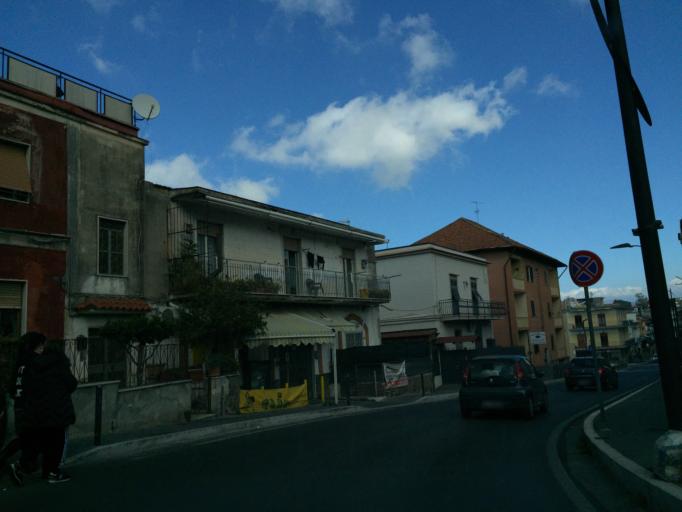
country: IT
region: Campania
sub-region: Provincia di Napoli
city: Massa di Somma
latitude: 40.8473
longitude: 14.3731
